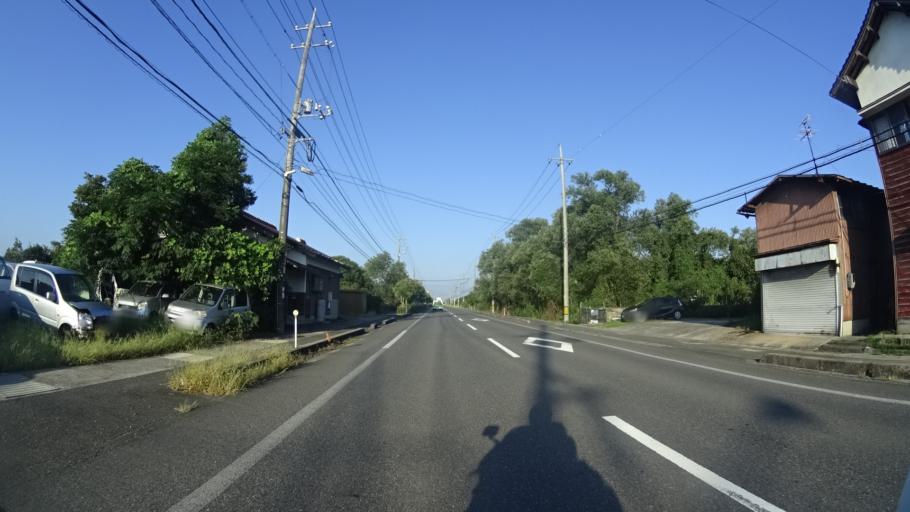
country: JP
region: Shimane
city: Sakaiminato
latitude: 35.5214
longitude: 133.2299
